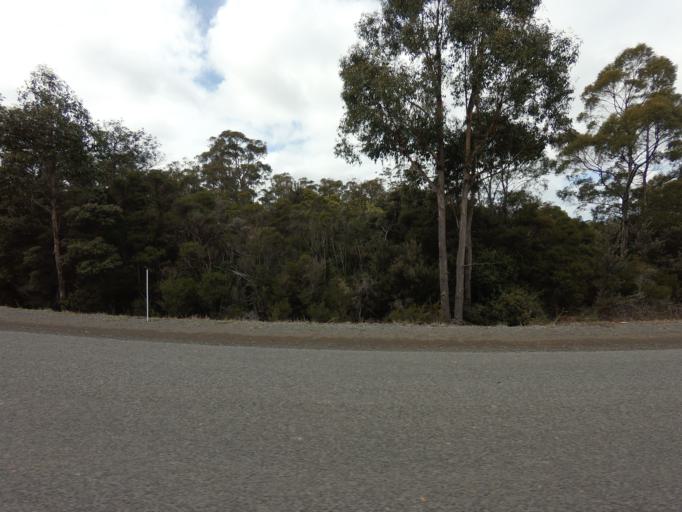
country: AU
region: Tasmania
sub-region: Huon Valley
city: Geeveston
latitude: -43.4217
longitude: 146.9051
